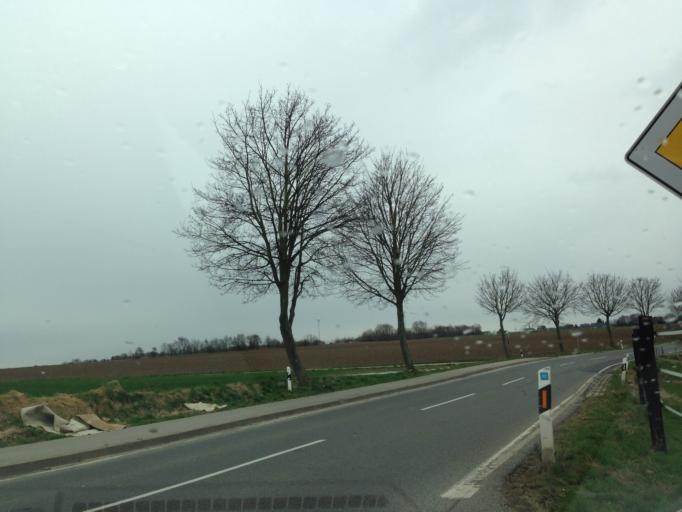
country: DE
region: North Rhine-Westphalia
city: Huckelhoven
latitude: 51.0805
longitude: 6.2439
